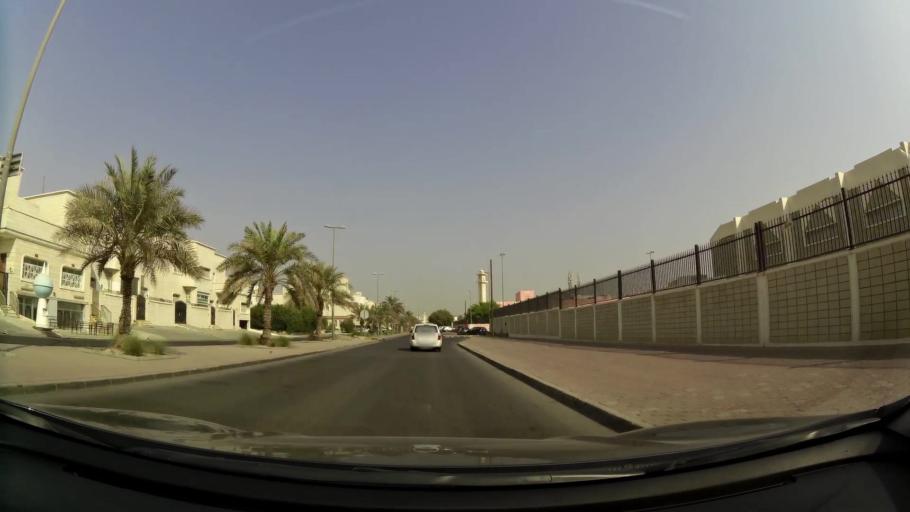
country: KW
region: Al Asimah
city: Ar Rabiyah
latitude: 29.2713
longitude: 47.8698
